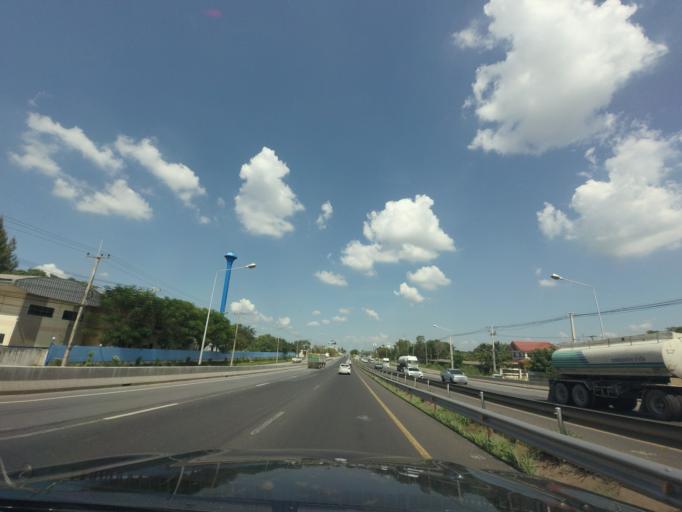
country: TH
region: Nakhon Ratchasima
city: Nakhon Ratchasima
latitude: 15.0585
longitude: 102.1667
